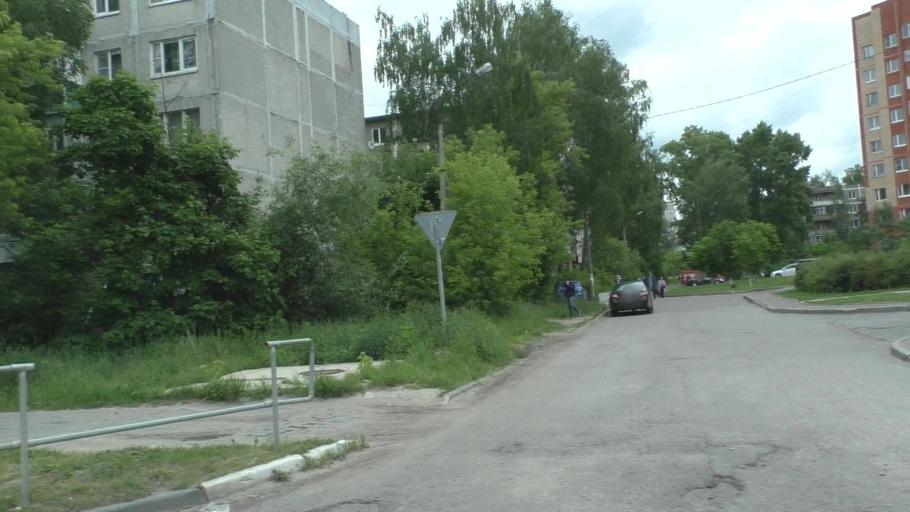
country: RU
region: Moskovskaya
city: Yegor'yevsk
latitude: 55.3681
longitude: 39.0549
